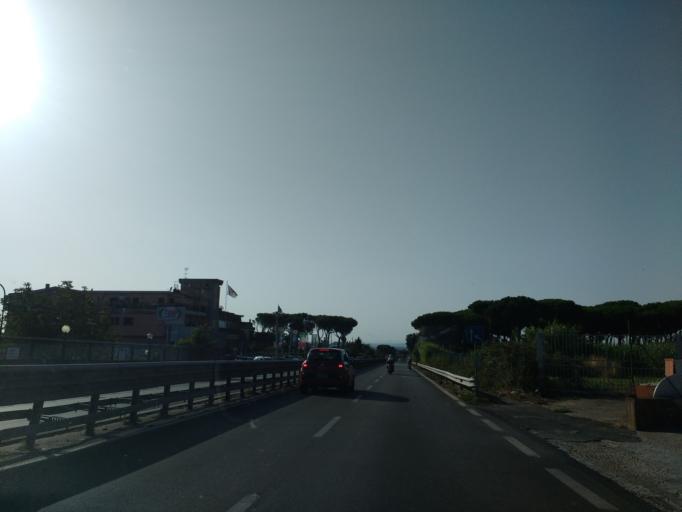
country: IT
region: Latium
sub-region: Citta metropolitana di Roma Capitale
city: Marino
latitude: 41.7591
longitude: 12.6250
